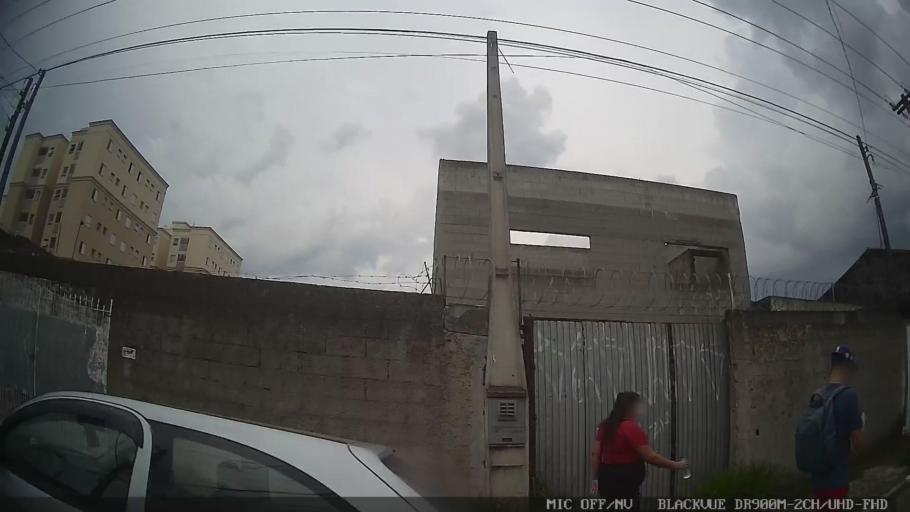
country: BR
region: Sao Paulo
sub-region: Suzano
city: Suzano
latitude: -23.5458
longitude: -46.2967
